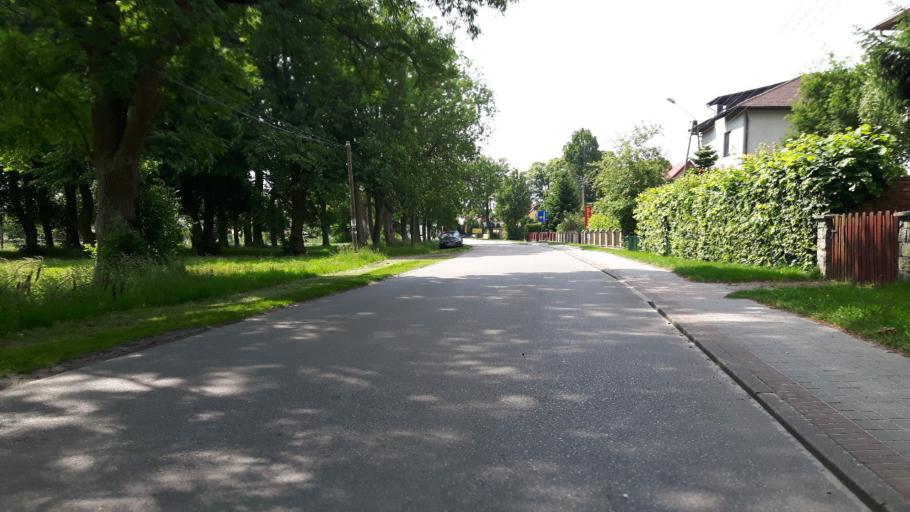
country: PL
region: Pomeranian Voivodeship
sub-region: Powiat leborski
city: Leba
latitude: 54.7518
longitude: 17.5879
